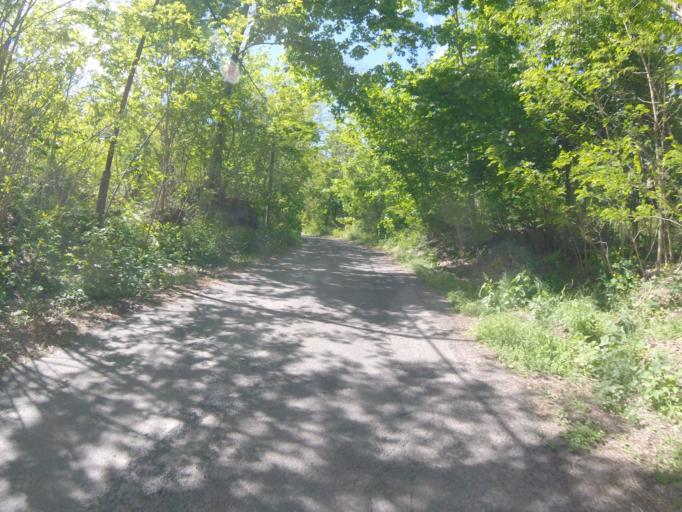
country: DE
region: Brandenburg
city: Teupitz
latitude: 52.1427
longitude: 13.5898
